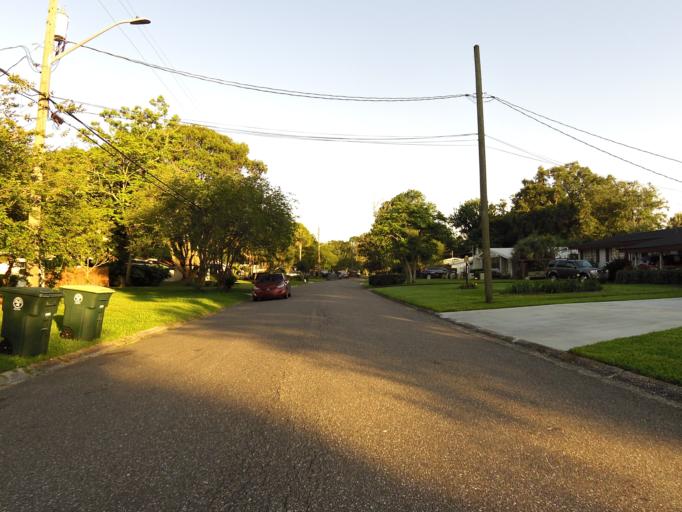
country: US
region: Florida
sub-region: Duval County
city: Jacksonville
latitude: 30.2351
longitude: -81.6107
